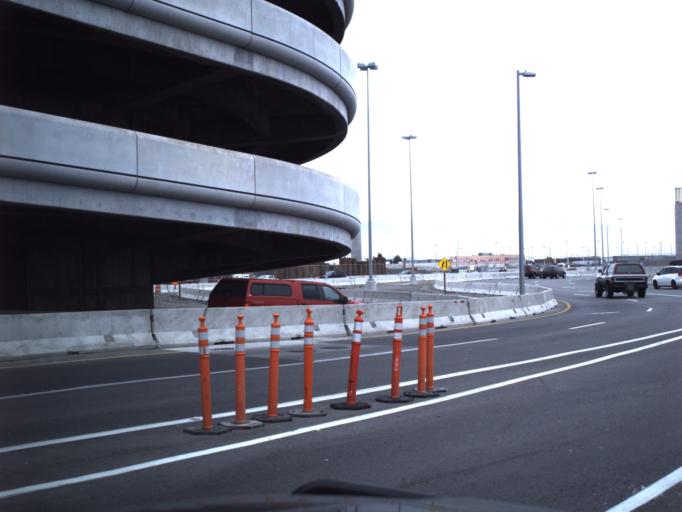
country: US
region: Utah
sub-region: Salt Lake County
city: West Valley City
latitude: 40.7851
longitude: -111.9837
